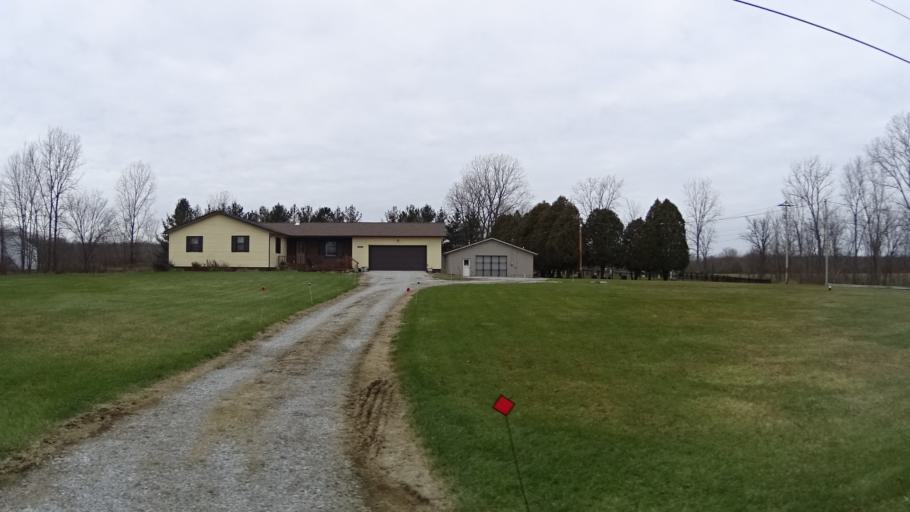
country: US
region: Ohio
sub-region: Lorain County
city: Wellington
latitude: 41.1483
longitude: -82.2692
